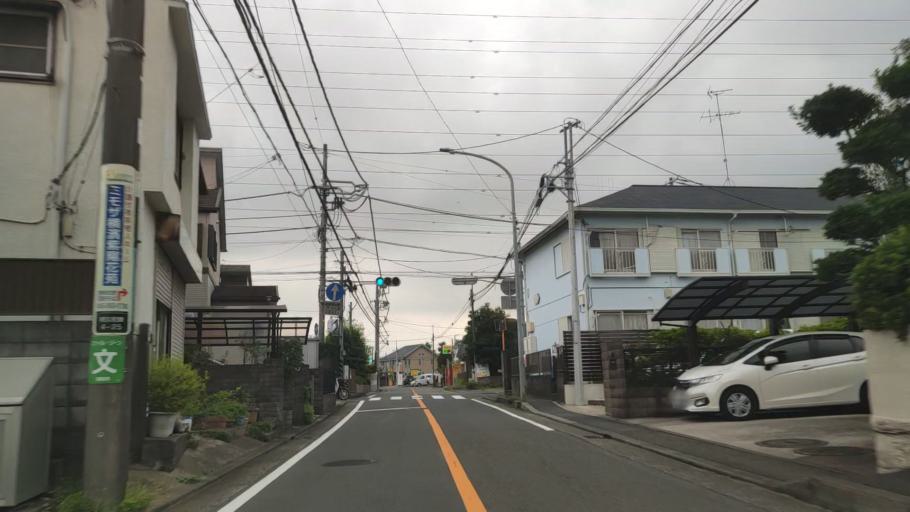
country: JP
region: Kanagawa
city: Minami-rinkan
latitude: 35.4488
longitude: 139.5006
